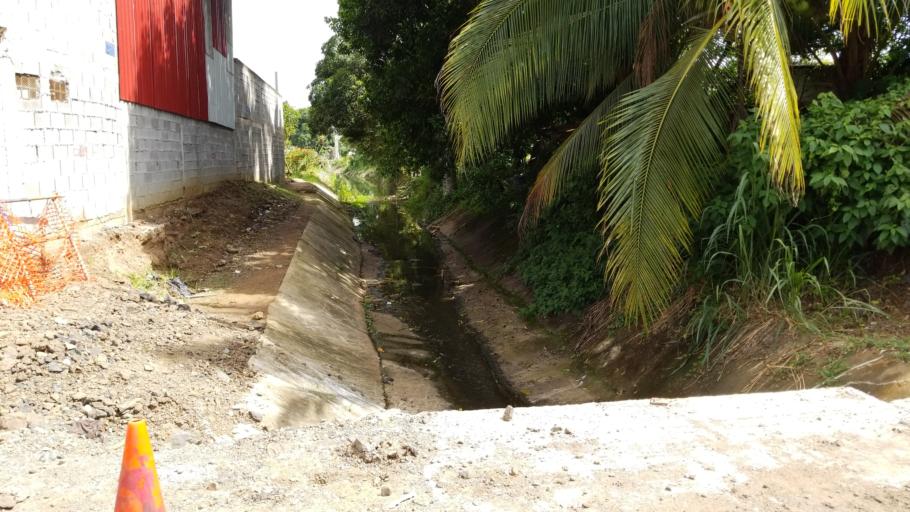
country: PA
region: Panama
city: San Miguelito
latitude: 9.0380
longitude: -79.4393
